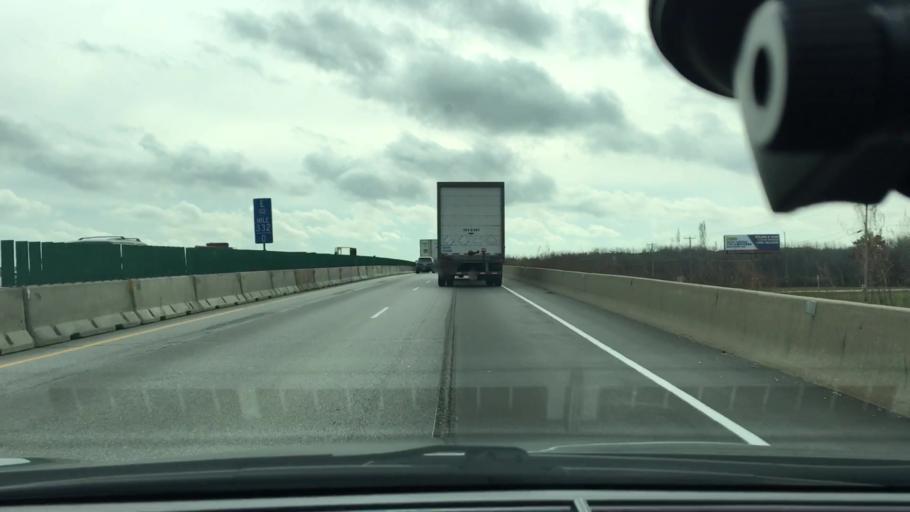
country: US
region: Wisconsin
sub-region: Racine County
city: Franksville
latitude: 42.7437
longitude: -87.9543
